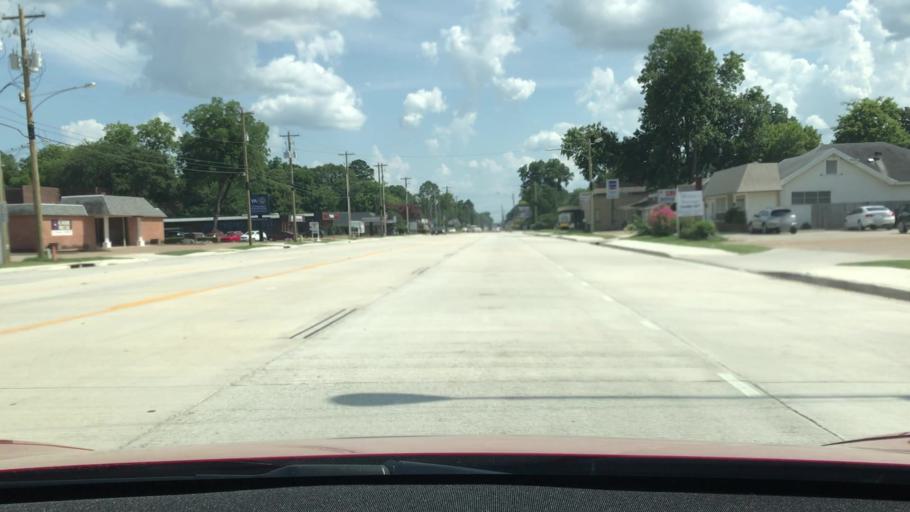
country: US
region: Louisiana
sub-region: Bossier Parish
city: Bossier City
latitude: 32.4790
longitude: -93.7222
